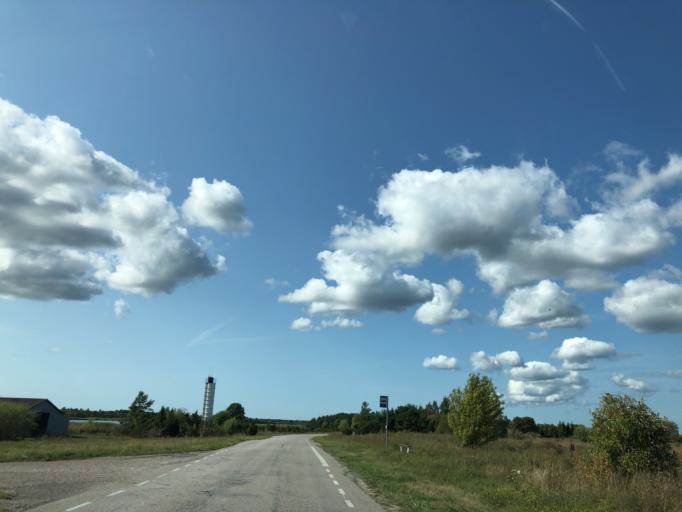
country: EE
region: Hiiumaa
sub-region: Kaerdla linn
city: Kardla
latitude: 58.7895
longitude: 22.7730
